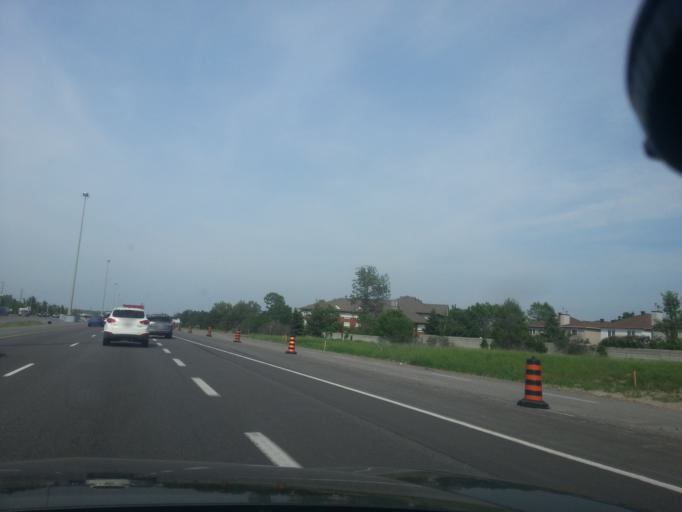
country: CA
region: Ontario
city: Bells Corners
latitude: 45.3068
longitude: -75.9091
